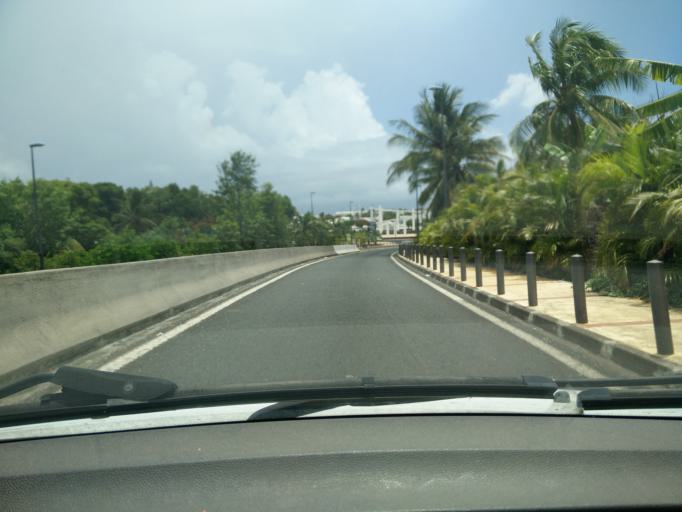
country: GP
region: Guadeloupe
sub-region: Guadeloupe
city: Pointe-a-Pitre
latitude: 16.2253
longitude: -61.5250
